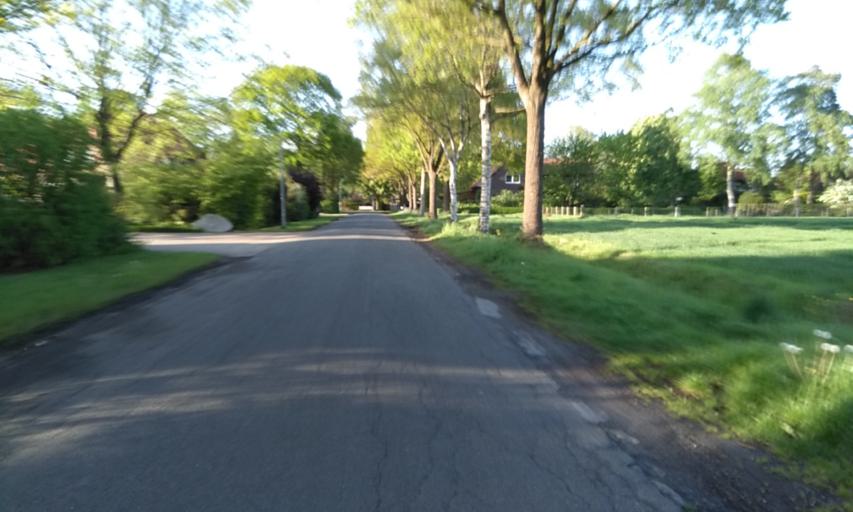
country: DE
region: Lower Saxony
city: Wohnste
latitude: 53.3932
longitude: 9.5054
